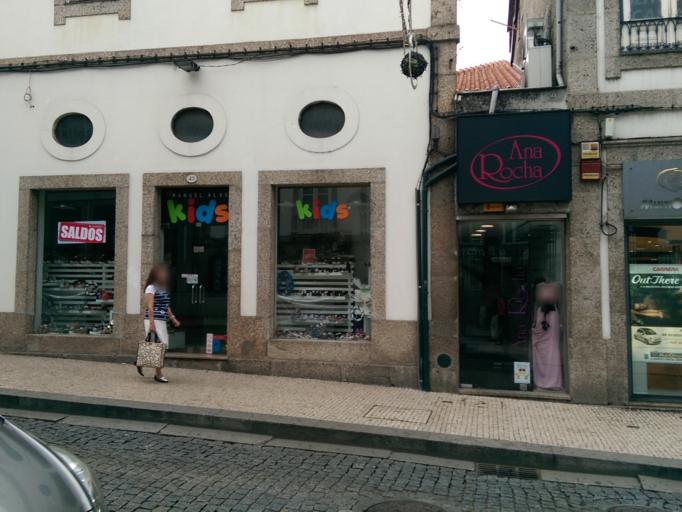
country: PT
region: Braga
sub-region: Guimaraes
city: Guimaraes
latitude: 41.4439
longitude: -8.2964
